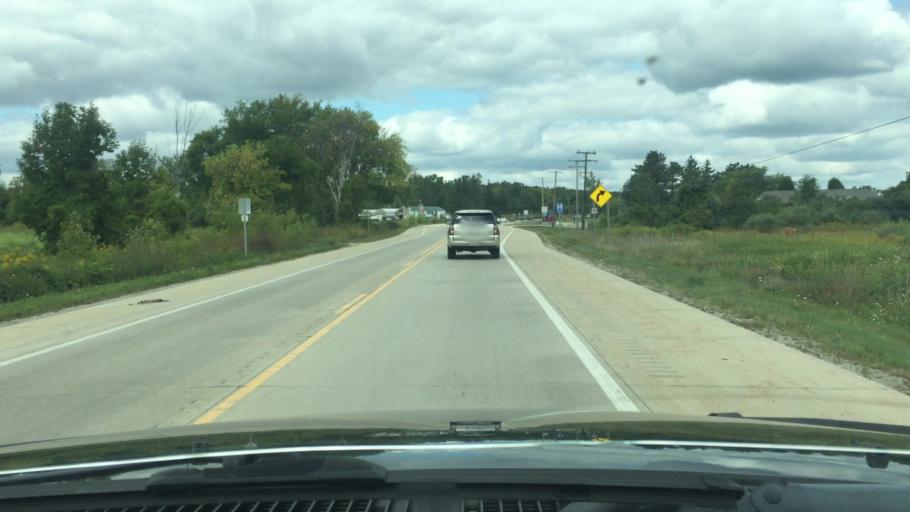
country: US
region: Michigan
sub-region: Lapeer County
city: Almont
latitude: 42.8850
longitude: -83.0385
